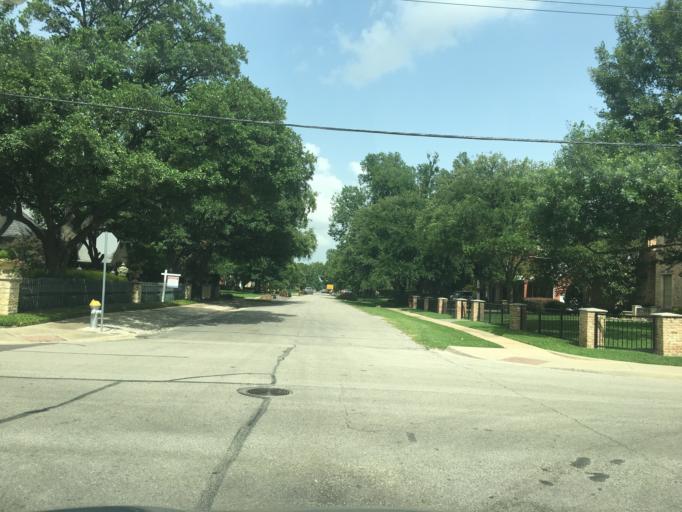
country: US
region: Texas
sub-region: Dallas County
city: University Park
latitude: 32.8843
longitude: -96.7934
